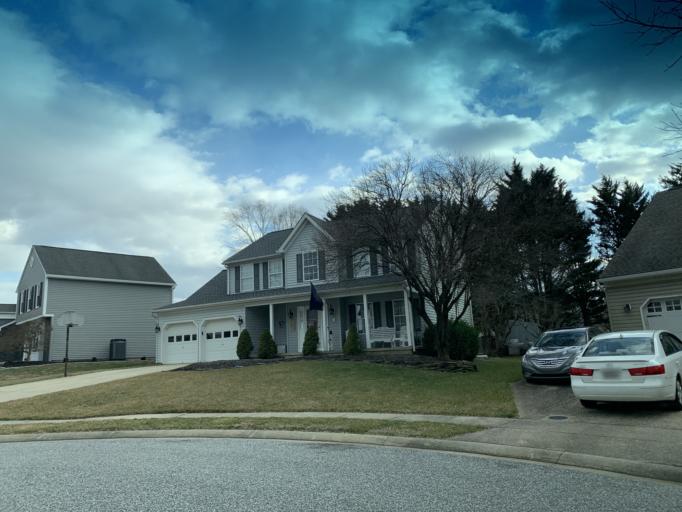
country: US
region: Maryland
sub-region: Harford County
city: South Bel Air
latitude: 39.5317
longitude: -76.3091
